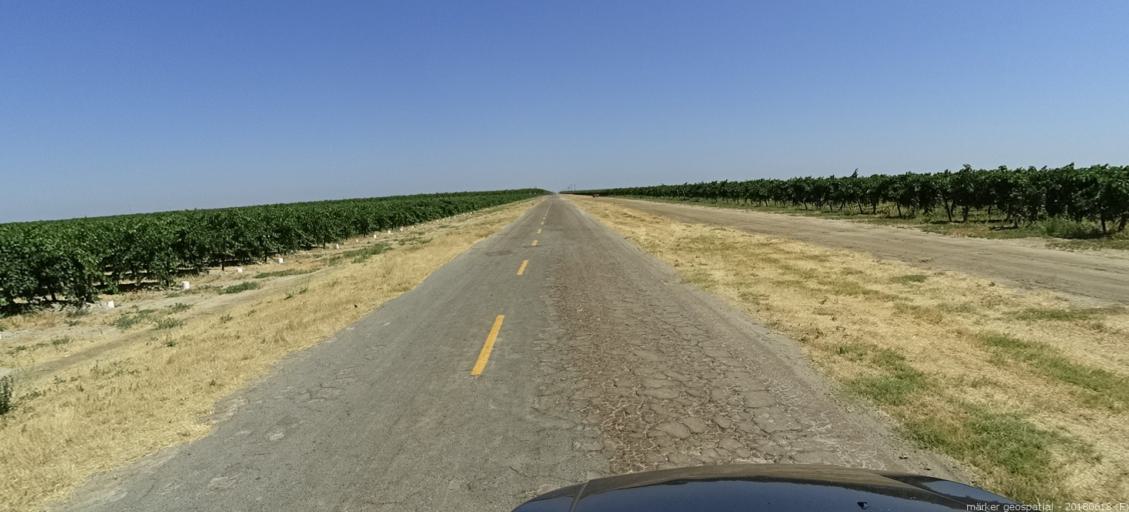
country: US
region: California
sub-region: Madera County
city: Parkwood
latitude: 36.8388
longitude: -120.1827
